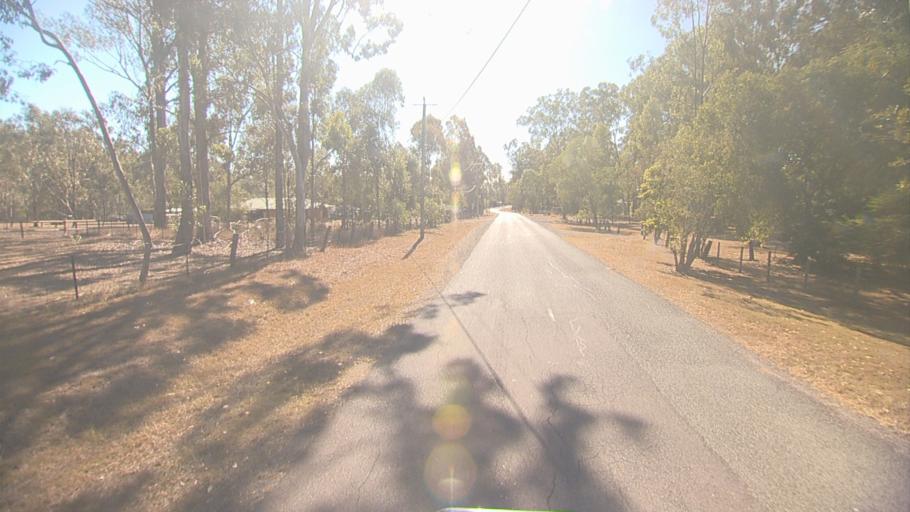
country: AU
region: Queensland
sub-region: Logan
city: Cedar Vale
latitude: -27.8856
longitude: 152.9999
